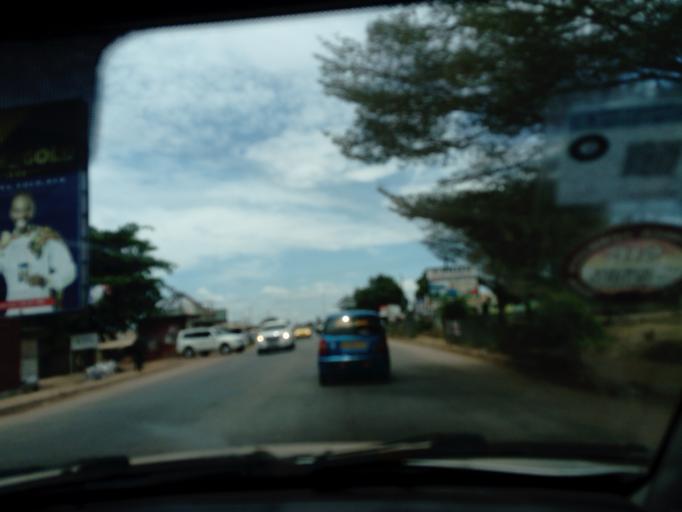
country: GH
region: Central
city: Cape Coast
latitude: 5.1245
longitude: -1.2705
